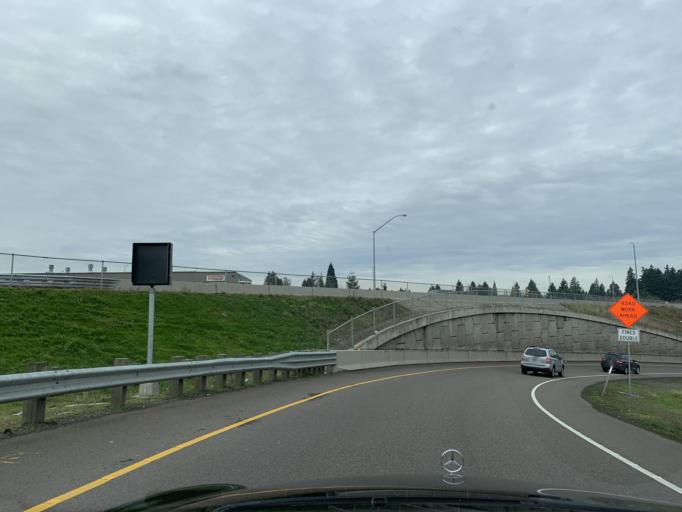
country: US
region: Oregon
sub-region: Clackamas County
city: Clackamas
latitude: 45.4184
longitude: -122.5719
